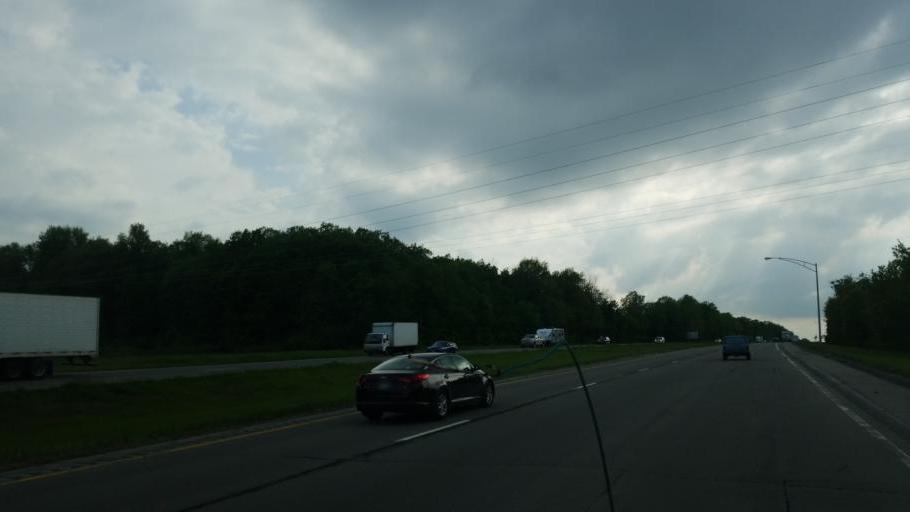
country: US
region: Ohio
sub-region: Richland County
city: Ontario
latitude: 40.7845
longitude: -82.5963
